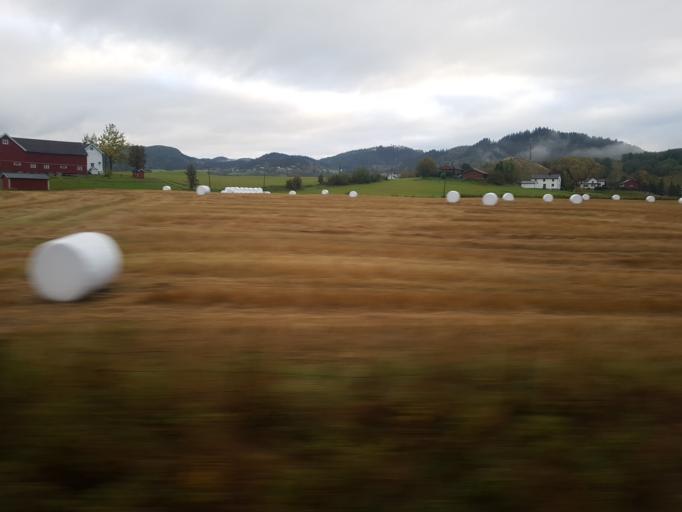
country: NO
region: Sor-Trondelag
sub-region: Melhus
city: Lundamo
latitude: 63.1892
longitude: 10.3086
